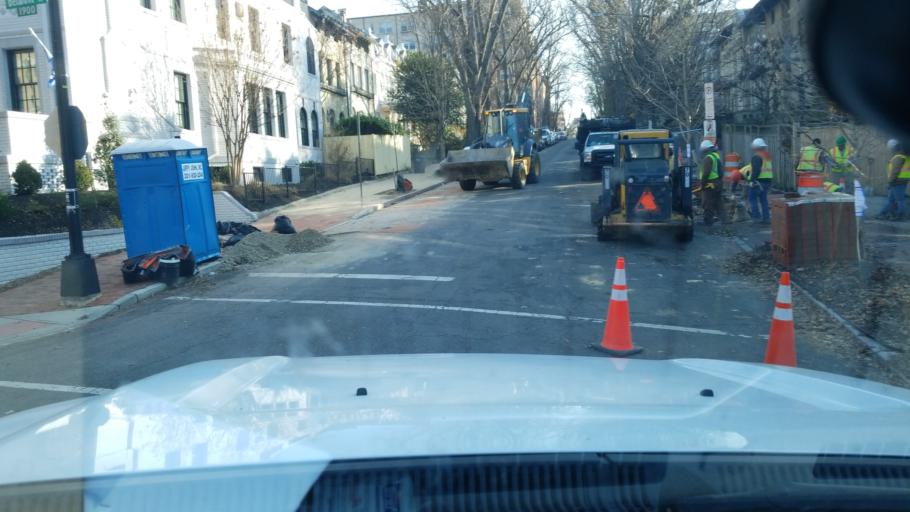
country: US
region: Washington, D.C.
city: Washington, D.C.
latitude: 38.9205
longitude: -77.0470
